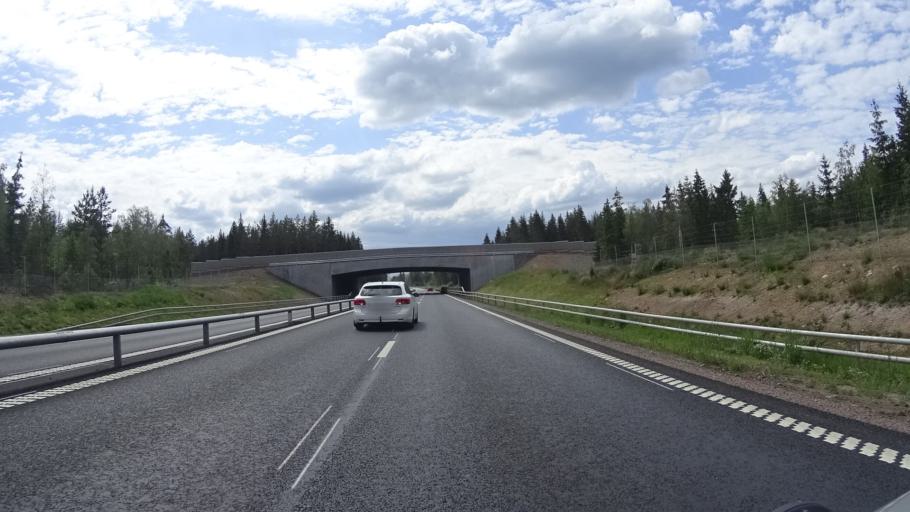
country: SE
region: Vaestra Goetaland
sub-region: Gullspangs Kommun
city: Hova
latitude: 58.8367
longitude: 14.1861
